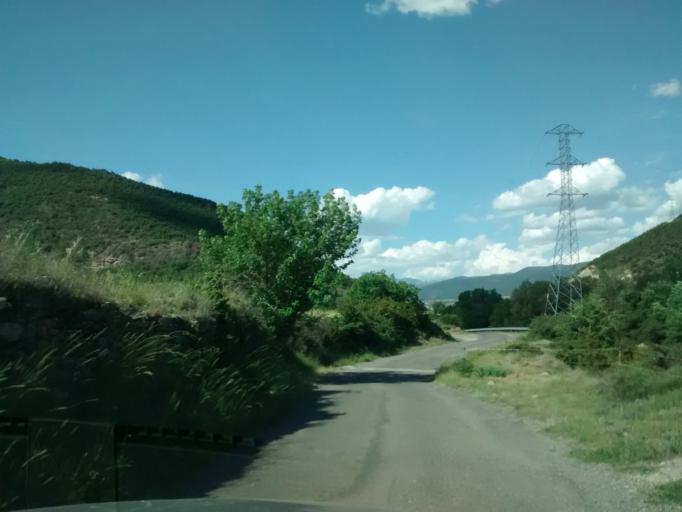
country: ES
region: Aragon
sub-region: Provincia de Huesca
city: Sabinanigo
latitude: 42.4884
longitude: -0.3746
